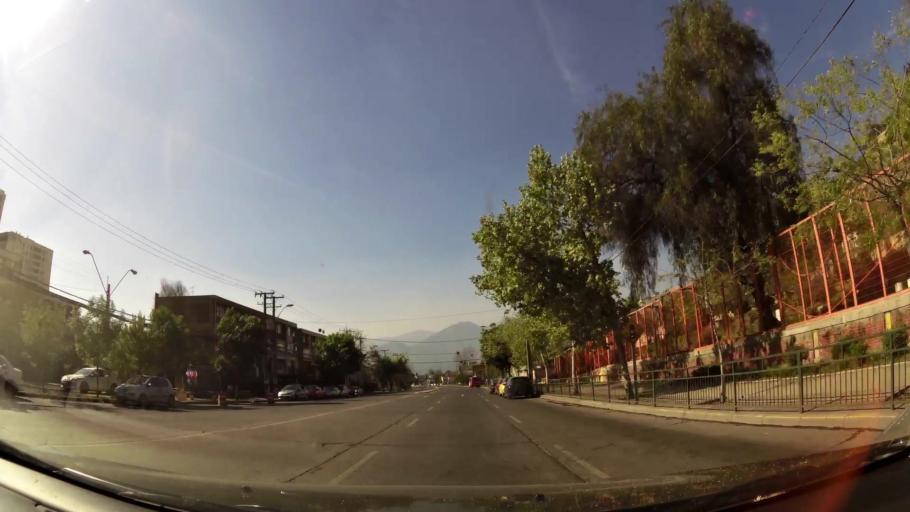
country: CL
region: Santiago Metropolitan
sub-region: Provincia de Santiago
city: Santiago
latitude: -33.4189
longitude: -70.6400
